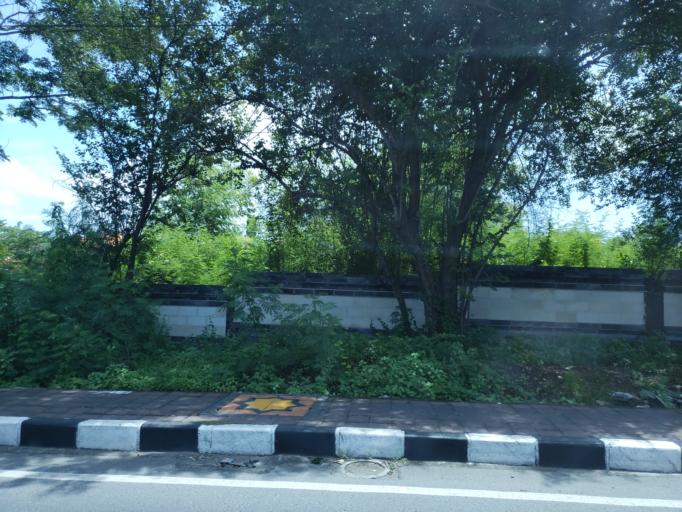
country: ID
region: Bali
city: Jimbaran
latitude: -8.8016
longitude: 115.1603
